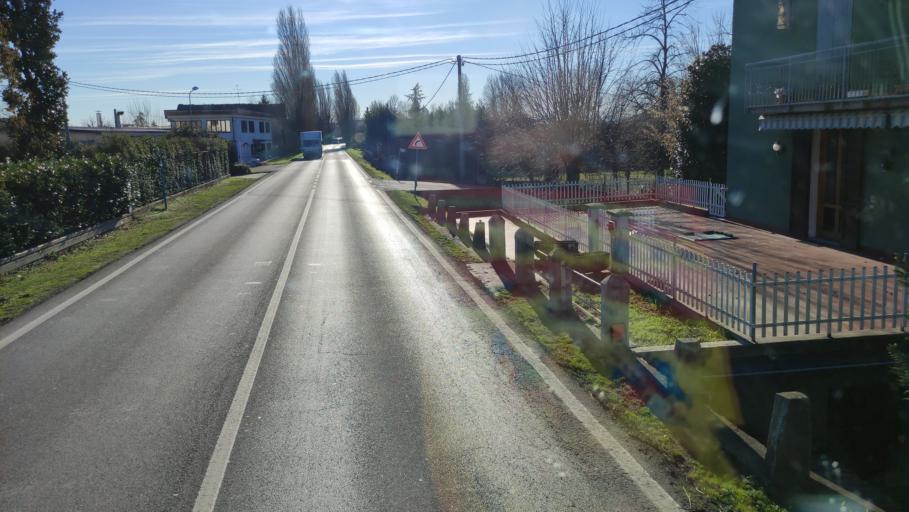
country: IT
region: Emilia-Romagna
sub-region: Provincia di Reggio Emilia
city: Novellara
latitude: 44.8401
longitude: 10.7176
